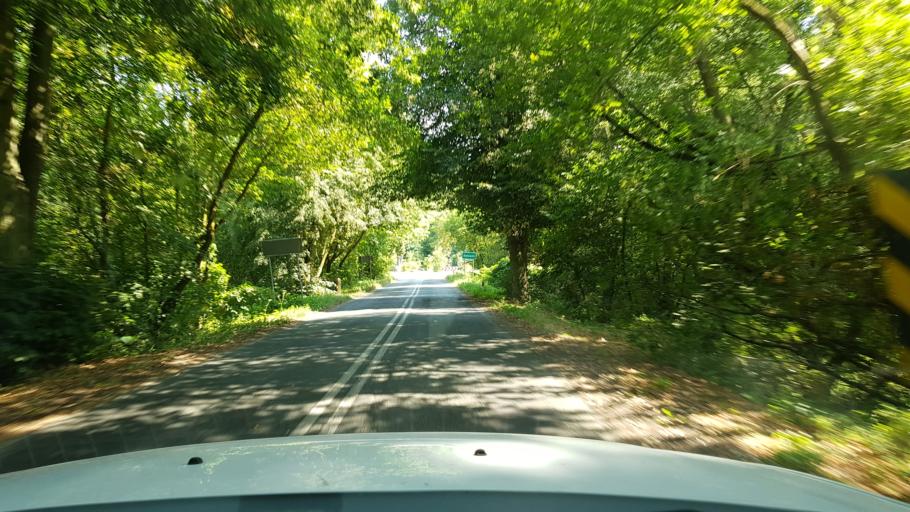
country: PL
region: West Pomeranian Voivodeship
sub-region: Powiat gryfinski
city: Cedynia
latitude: 52.8213
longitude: 14.2330
